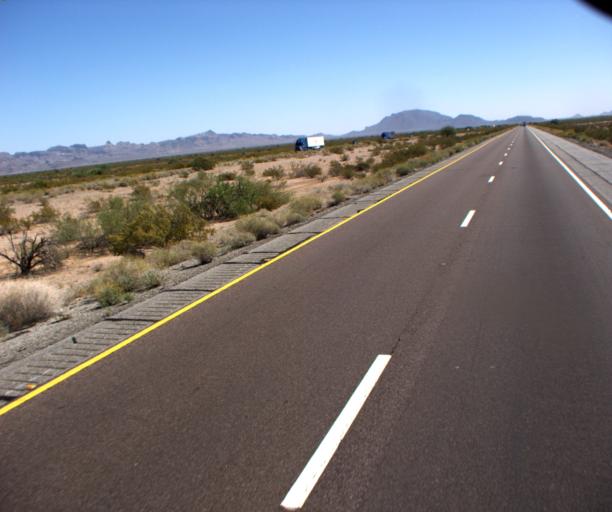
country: US
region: Arizona
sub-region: La Paz County
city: Salome
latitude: 33.5507
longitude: -113.2342
